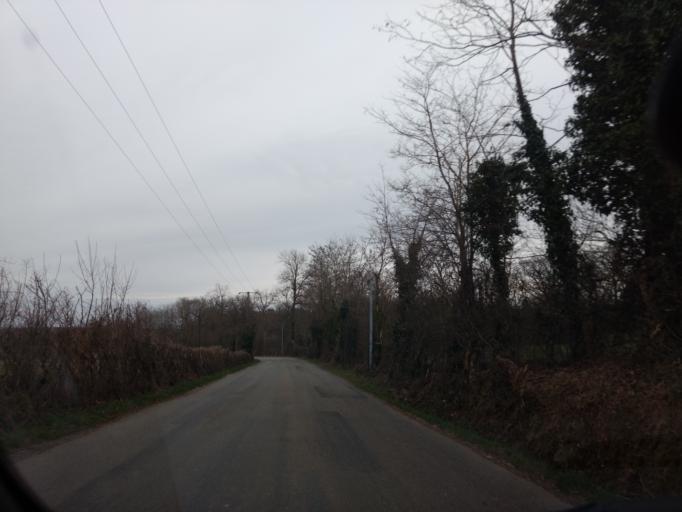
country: FR
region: Midi-Pyrenees
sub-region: Departement de l'Aveyron
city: Saint-Christophe-Vallon
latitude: 44.4322
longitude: 2.3534
